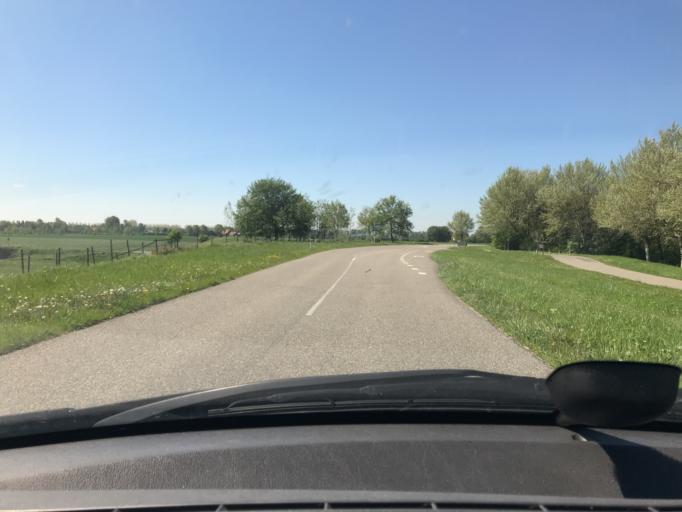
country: NL
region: Zeeland
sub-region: Gemeente Goes
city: Goes
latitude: 51.5406
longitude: 3.8020
